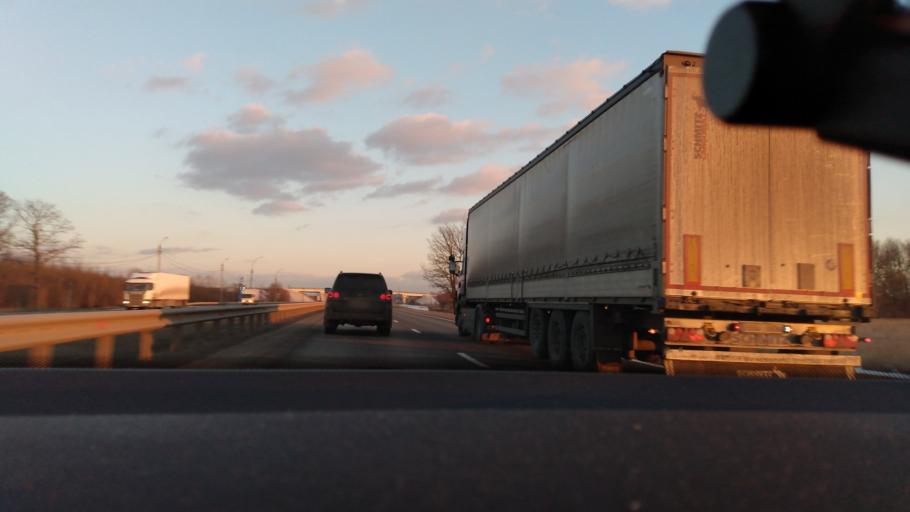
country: RU
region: Moskovskaya
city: Raduzhnyy
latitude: 55.1475
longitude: 38.7226
